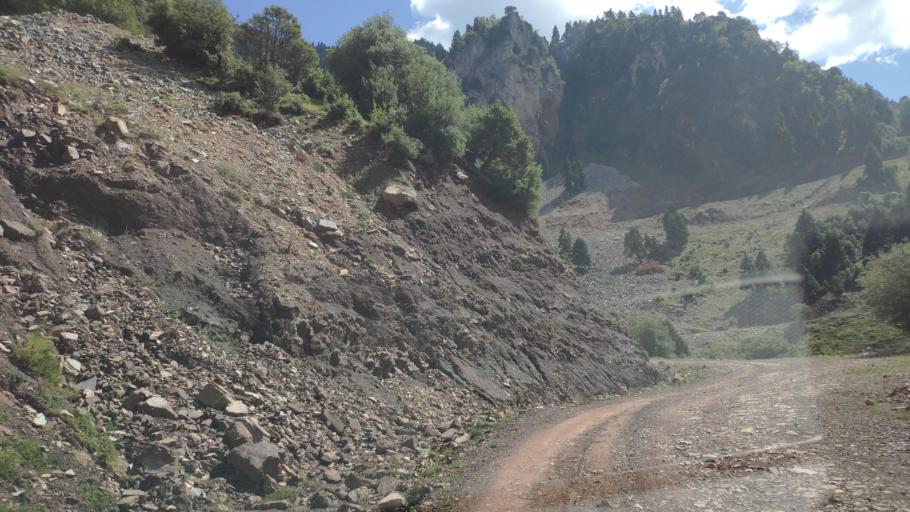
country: GR
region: Central Greece
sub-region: Nomos Evrytanias
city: Kerasochori
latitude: 39.1390
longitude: 21.6588
